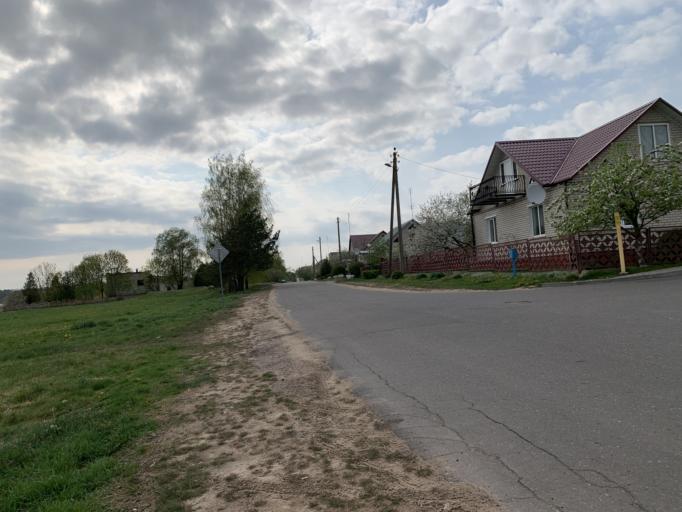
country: BY
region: Minsk
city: Nyasvizh
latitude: 53.2125
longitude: 26.6750
